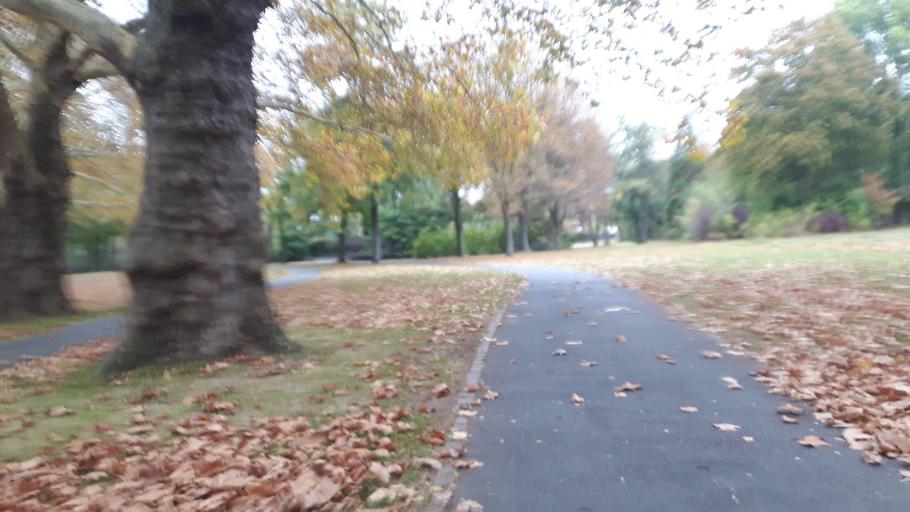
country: DE
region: North Rhine-Westphalia
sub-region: Regierungsbezirk Koln
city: Bonn
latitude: 50.7232
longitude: 7.1310
